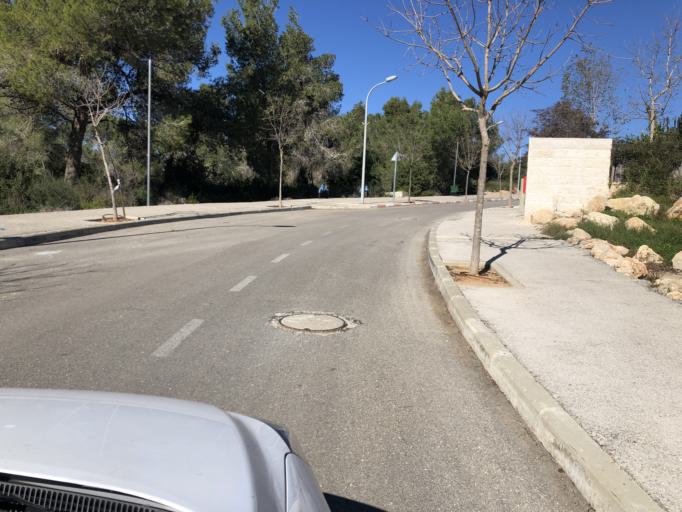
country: IL
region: Jerusalem
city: Zur Hadassa
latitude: 31.7434
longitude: 35.0515
